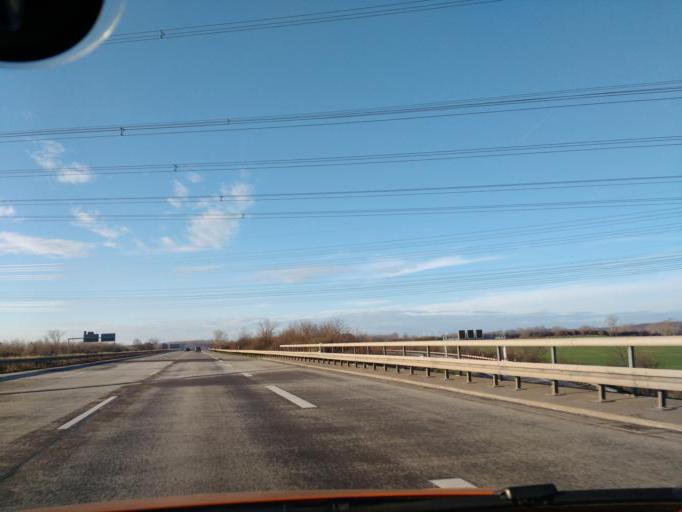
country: DE
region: Saxony-Anhalt
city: Dahlenwarsleben
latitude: 52.1678
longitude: 11.5380
